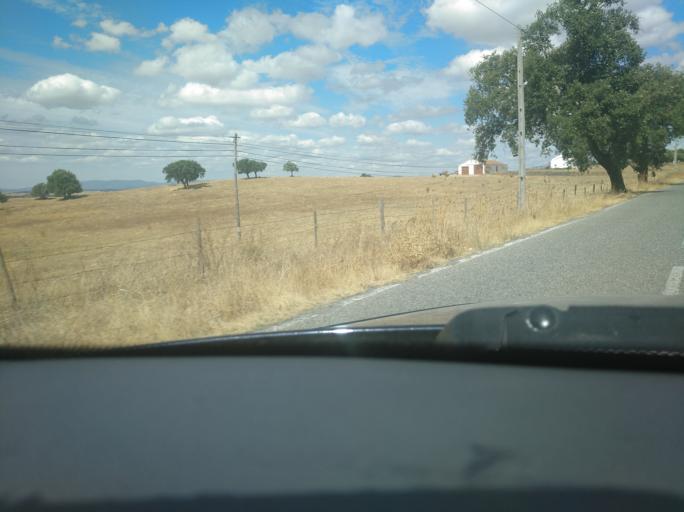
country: PT
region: Portalegre
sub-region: Arronches
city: Arronches
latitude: 39.0628
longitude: -7.4084
